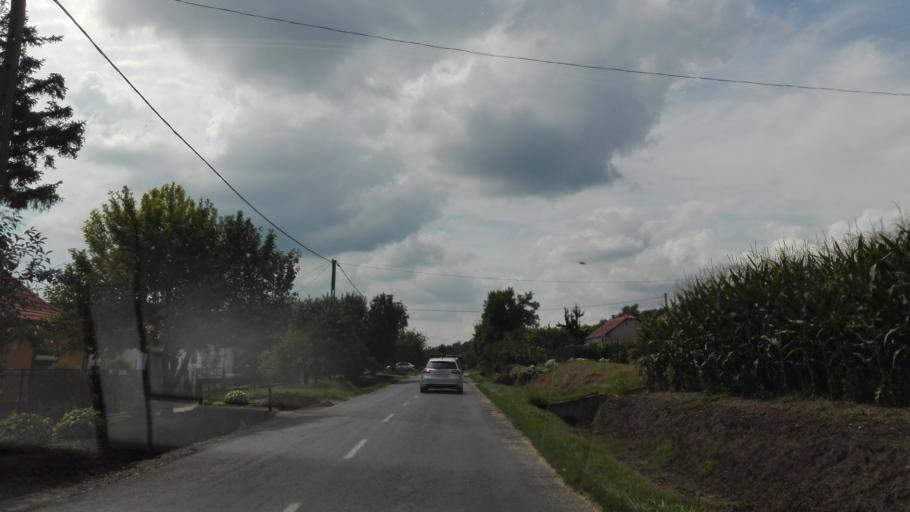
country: HU
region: Fejer
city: Mezoszilas
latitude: 46.7513
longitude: 18.4725
